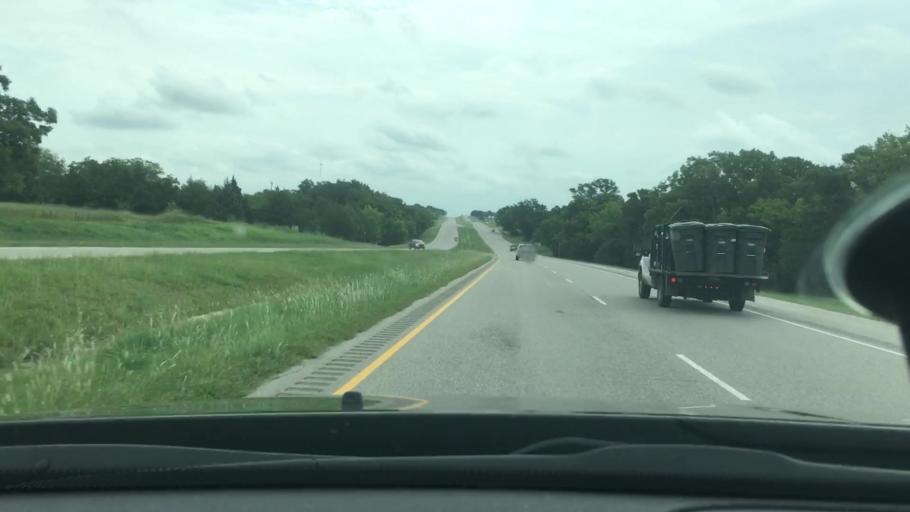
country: US
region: Oklahoma
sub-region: Carter County
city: Wilson
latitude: 34.1730
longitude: -97.4241
